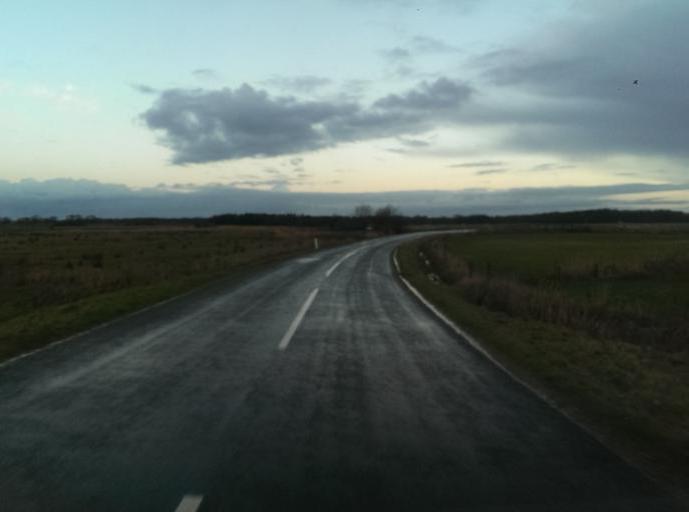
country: DK
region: South Denmark
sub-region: Esbjerg Kommune
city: Tjaereborg
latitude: 55.4592
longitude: 8.6394
